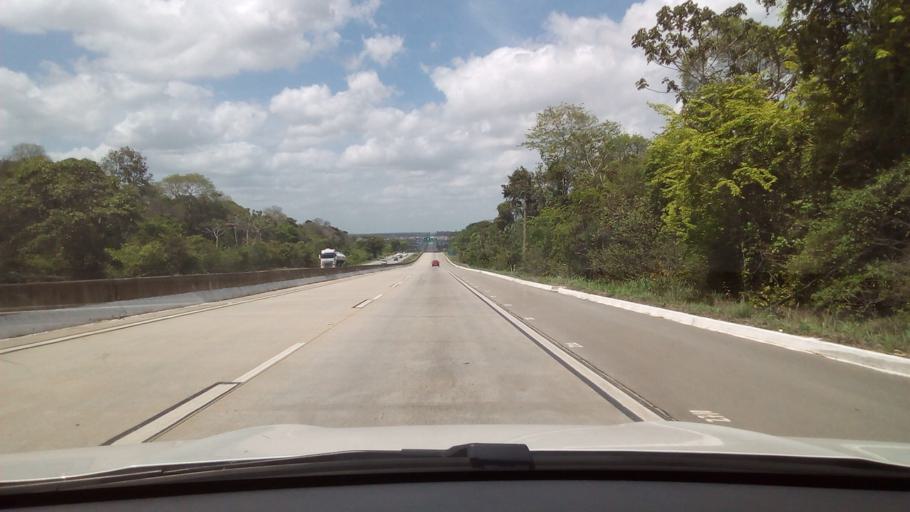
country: BR
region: Paraiba
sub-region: Mamanguape
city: Mamanguape
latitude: -6.8729
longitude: -35.1324
